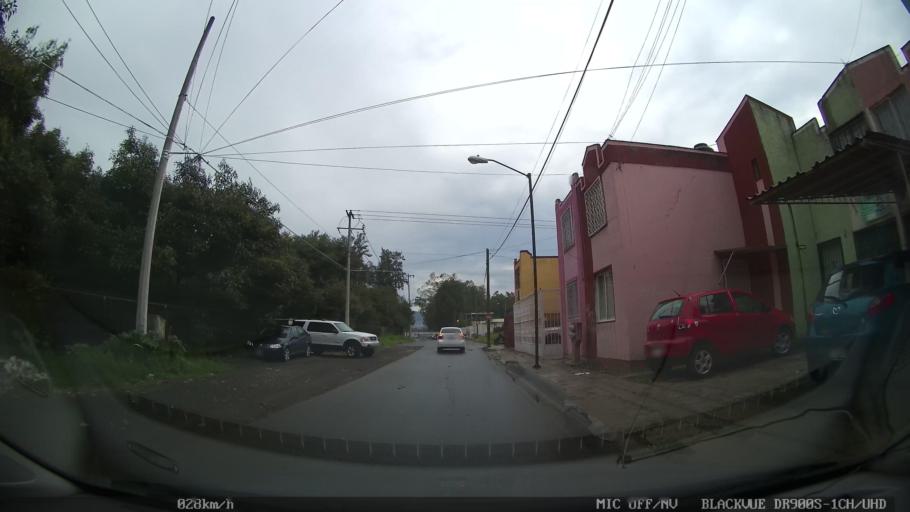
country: MX
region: Michoacan
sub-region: Uruapan
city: Santa Rosa (Santa Barbara)
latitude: 19.4023
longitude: -102.0303
